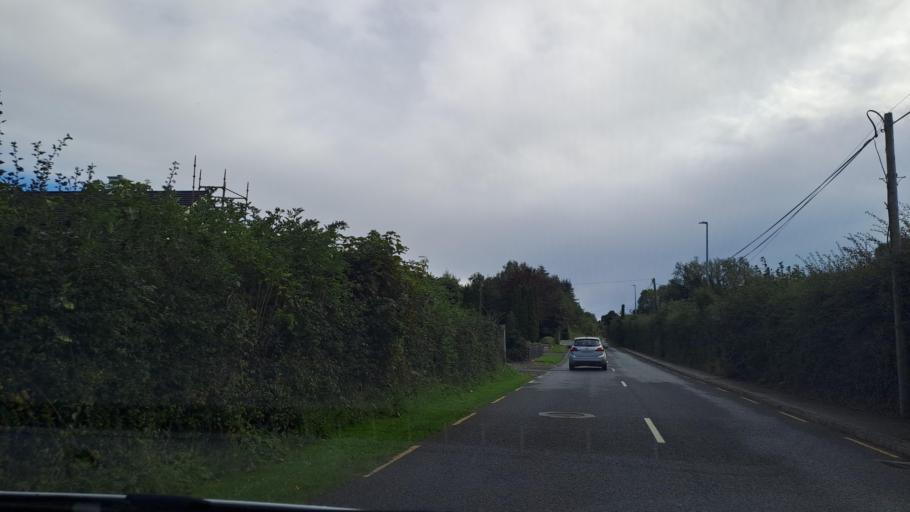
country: IE
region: Ulster
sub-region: County Monaghan
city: Carrickmacross
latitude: 53.9616
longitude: -6.7056
